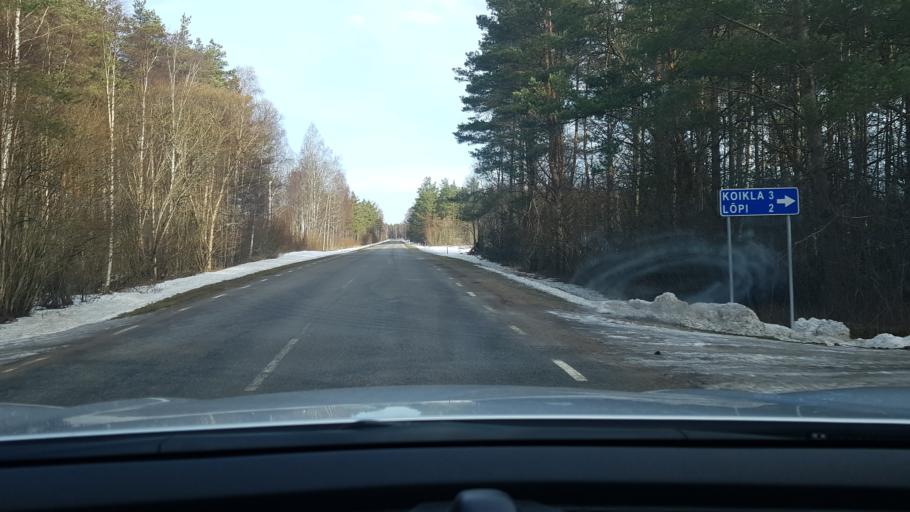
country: EE
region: Saare
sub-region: Kuressaare linn
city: Kuressaare
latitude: 58.4818
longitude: 22.7050
